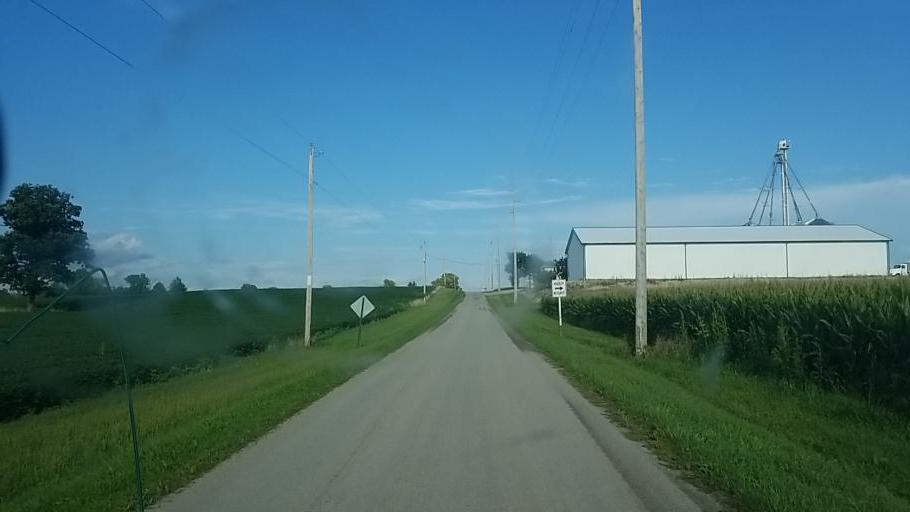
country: US
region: Ohio
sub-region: Wyandot County
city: Upper Sandusky
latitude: 40.8146
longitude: -83.2199
